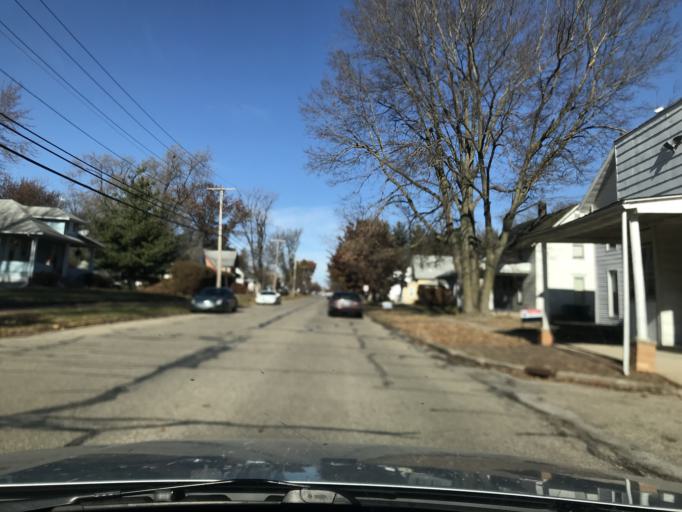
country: US
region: Illinois
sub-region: McDonough County
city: Macomb
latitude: 40.4532
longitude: -90.6673
